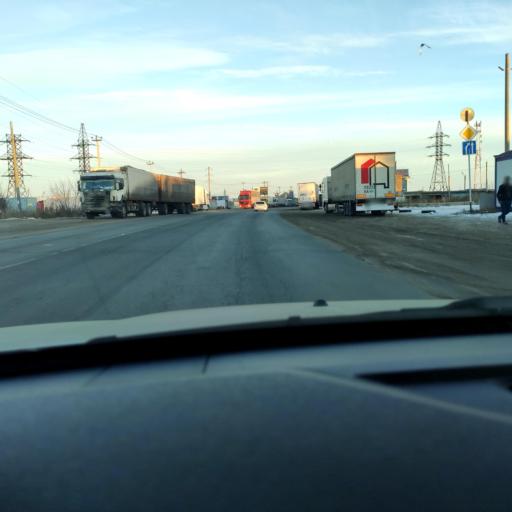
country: RU
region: Samara
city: Smyshlyayevka
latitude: 53.2483
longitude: 50.4746
